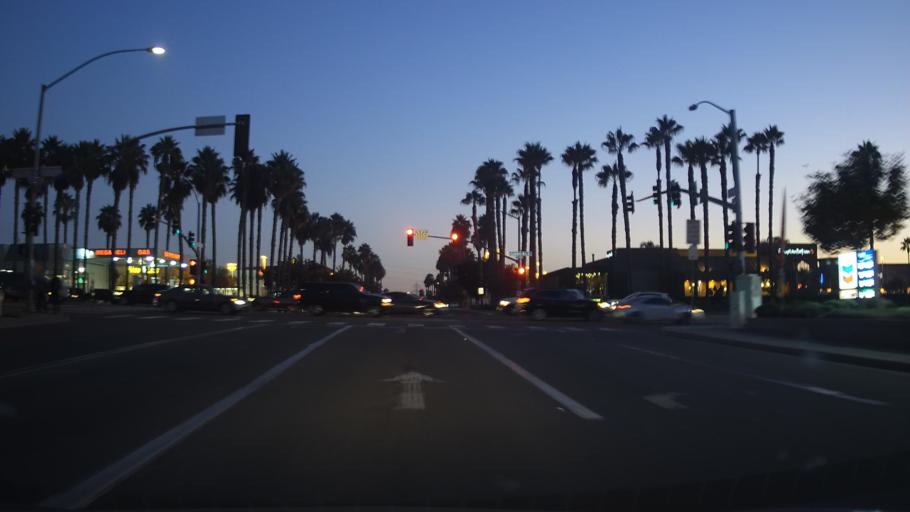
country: US
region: California
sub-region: San Diego County
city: La Jolla
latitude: 32.8331
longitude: -117.1639
